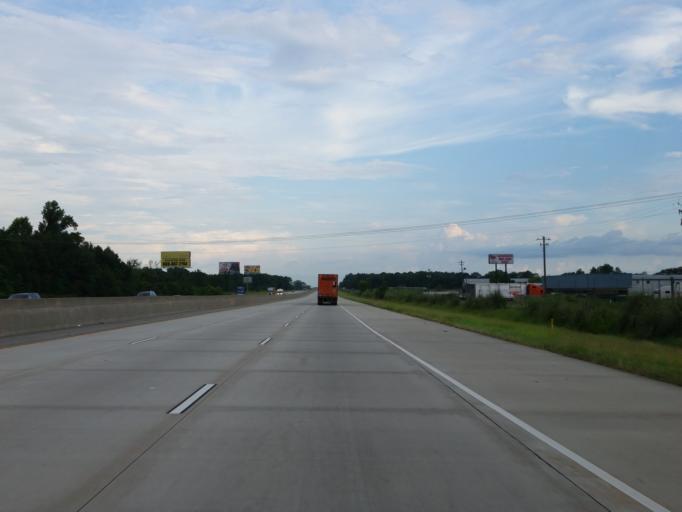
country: US
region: Georgia
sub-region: Cook County
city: Adel
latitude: 31.1060
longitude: -83.4245
